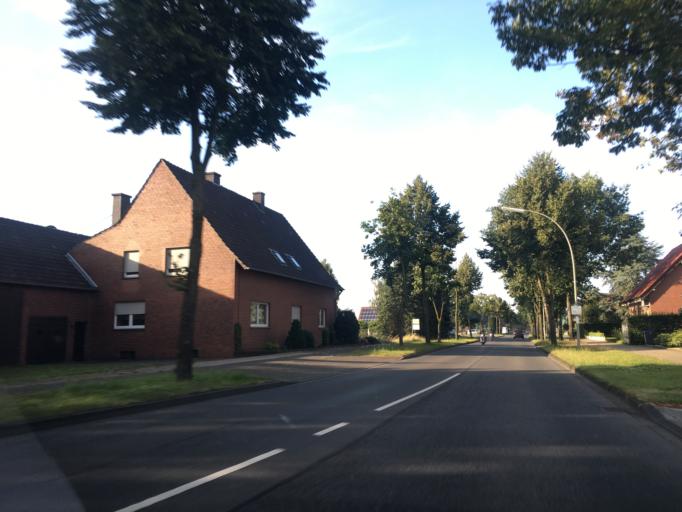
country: DE
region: North Rhine-Westphalia
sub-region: Regierungsbezirk Munster
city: Dulmen
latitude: 51.8065
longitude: 7.2422
